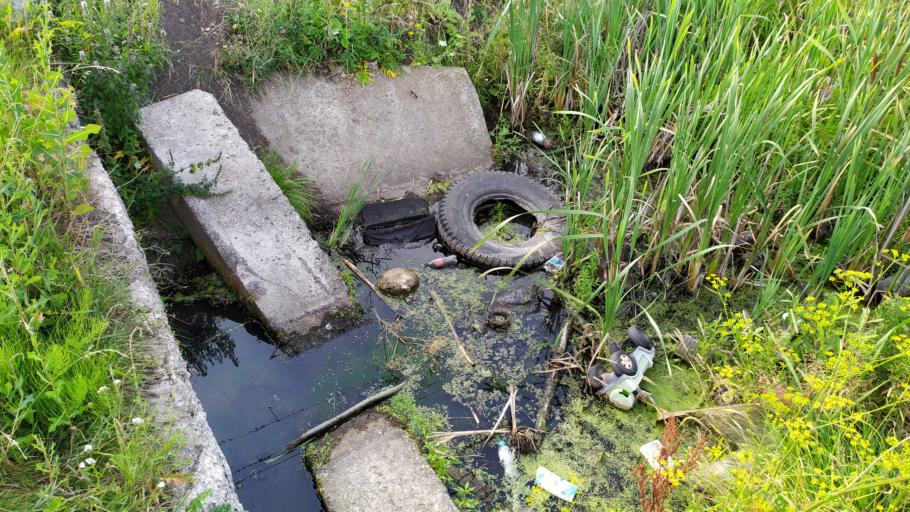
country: RU
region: Kursk
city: Kursk
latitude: 51.6430
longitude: 36.1628
